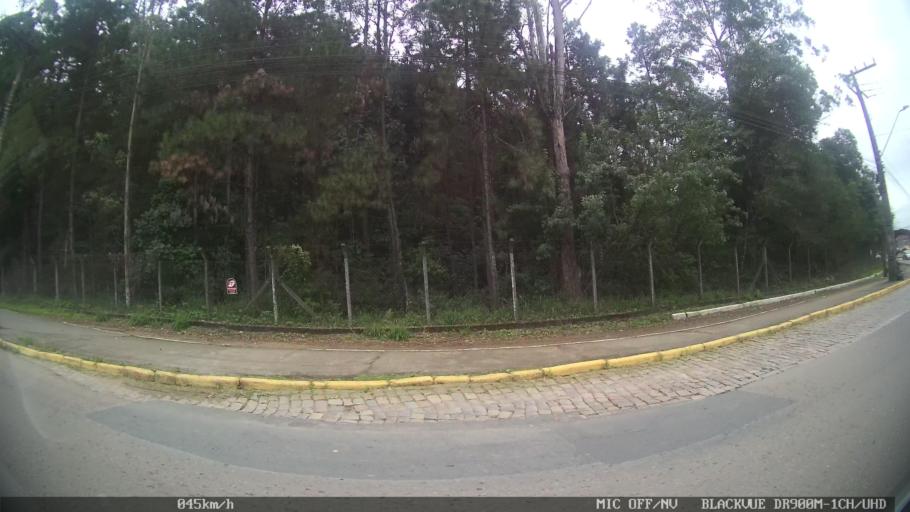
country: BR
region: Santa Catarina
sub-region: Joinville
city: Joinville
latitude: -26.2844
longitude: -48.8105
